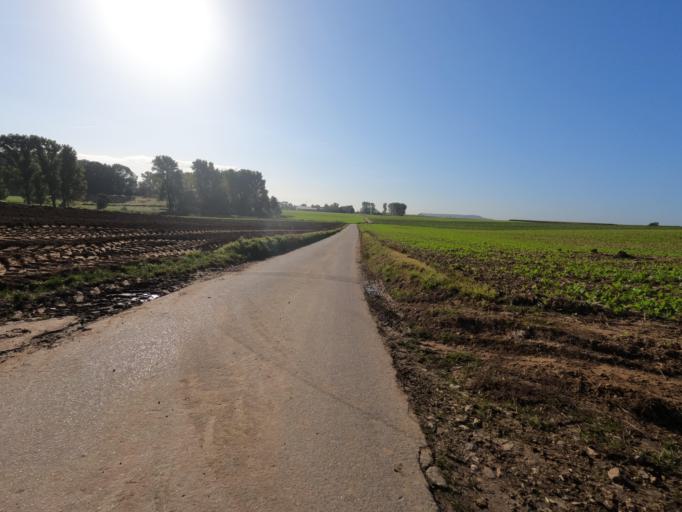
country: DE
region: North Rhine-Westphalia
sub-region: Regierungsbezirk Koln
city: Linnich
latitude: 50.9695
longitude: 6.2543
